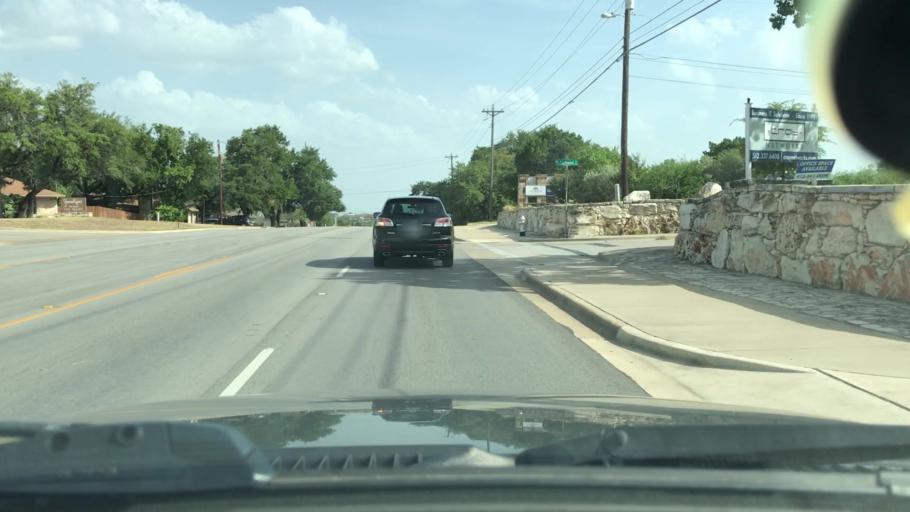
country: US
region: Texas
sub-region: Williamson County
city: Leander
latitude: 30.5442
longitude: -97.8510
